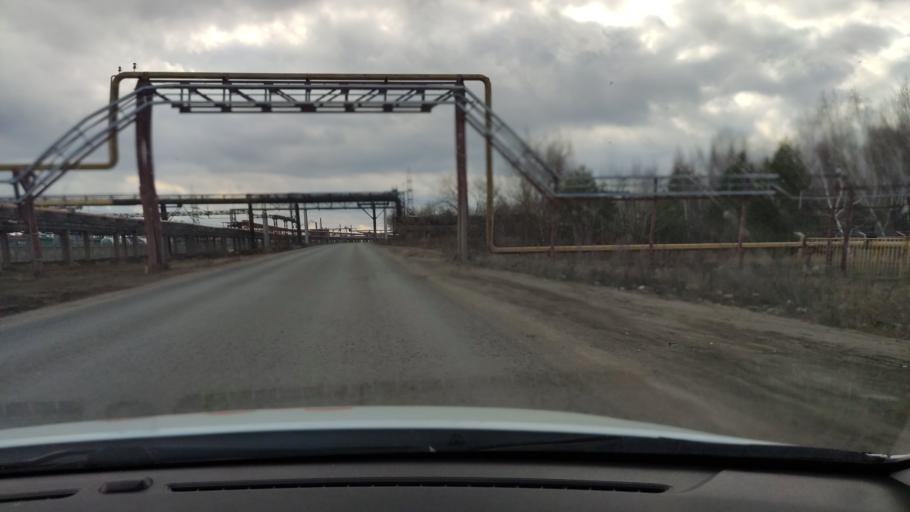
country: RU
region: Tatarstan
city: Staroye Arakchino
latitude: 55.8807
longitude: 48.9761
